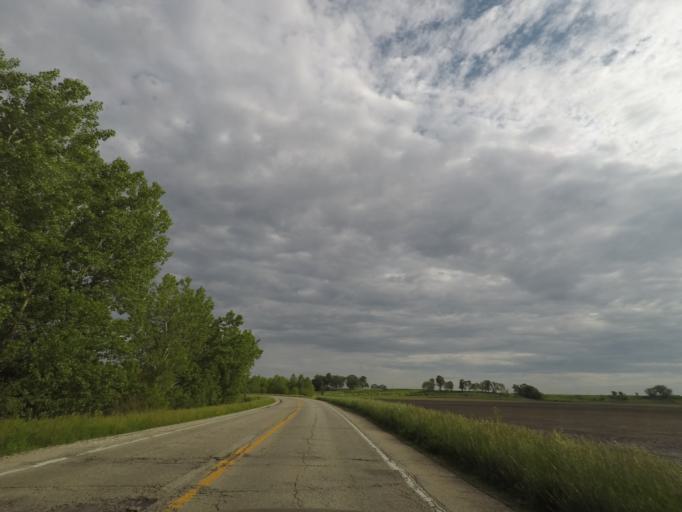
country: US
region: Illinois
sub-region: Logan County
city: Mount Pulaski
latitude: 40.0579
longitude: -89.2820
